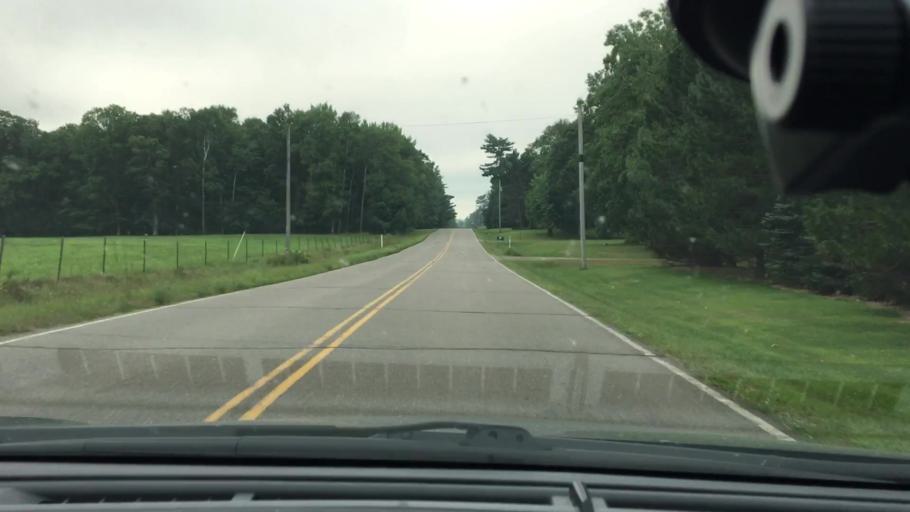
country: US
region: Minnesota
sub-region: Crow Wing County
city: Cross Lake
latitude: 46.6436
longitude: -94.0096
